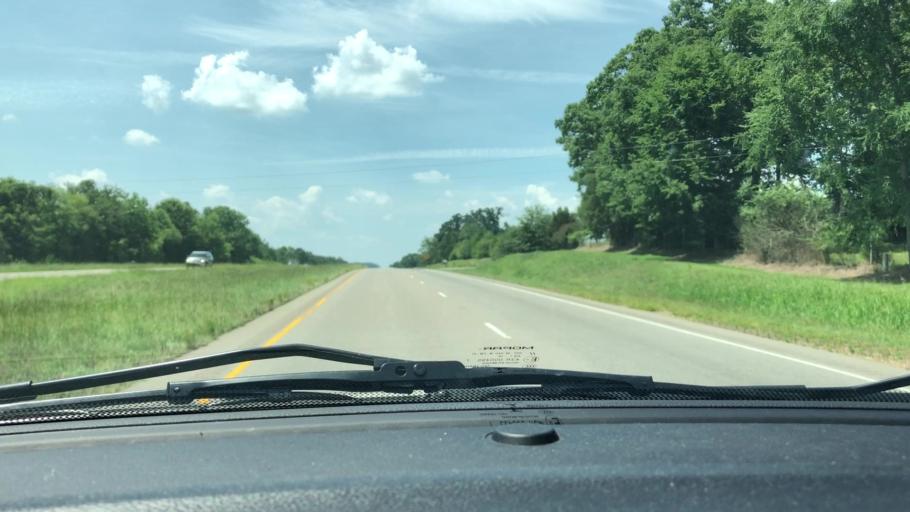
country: US
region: North Carolina
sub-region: Chatham County
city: Farmville
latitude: 35.6136
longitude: -79.3455
